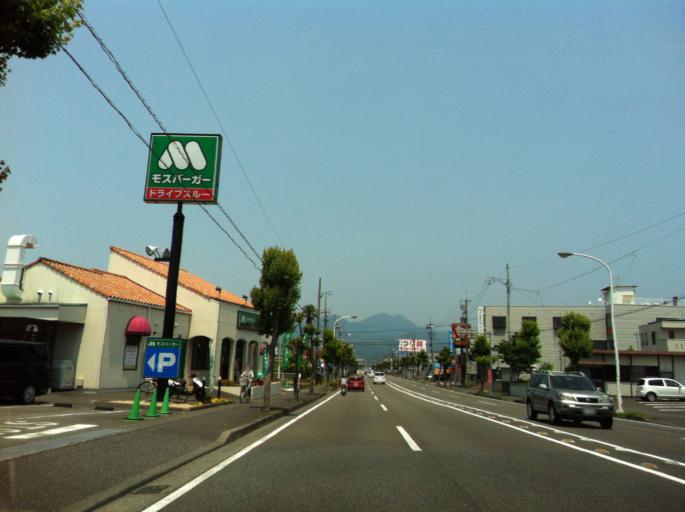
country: JP
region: Shizuoka
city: Shizuoka-shi
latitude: 34.9761
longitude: 138.4247
